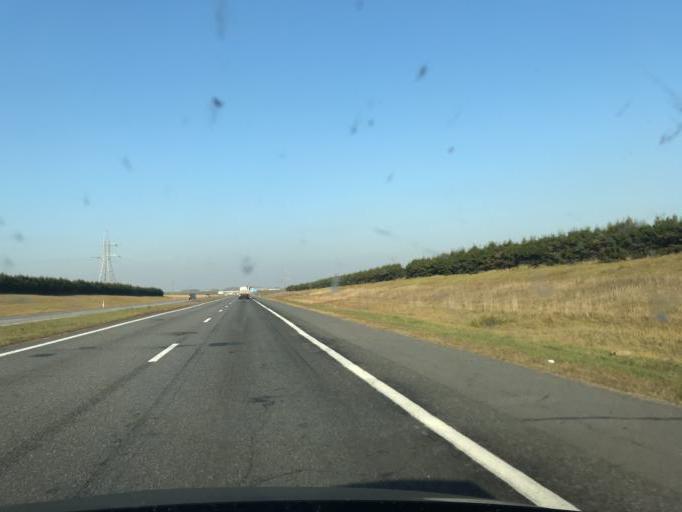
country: BY
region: Grodnenskaya
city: Mir
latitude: 53.4361
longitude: 26.5882
